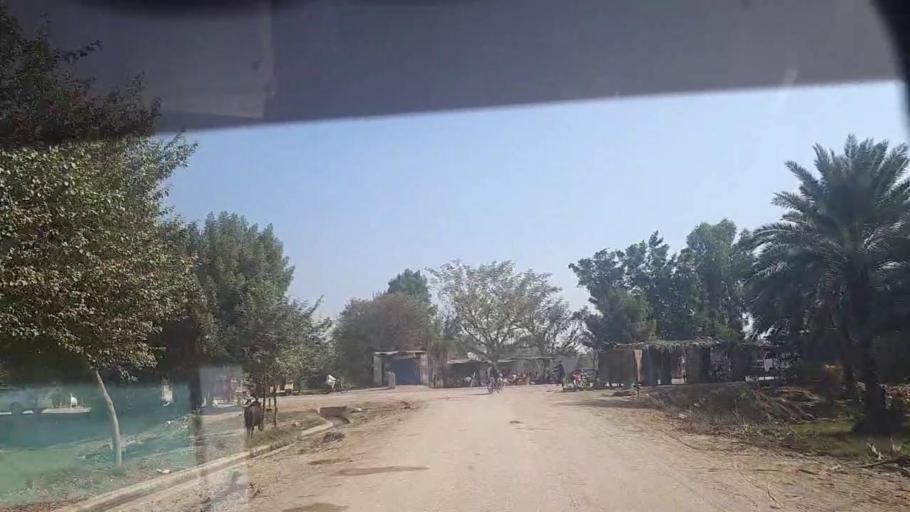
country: PK
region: Sindh
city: Khairpur
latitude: 27.4573
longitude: 68.7539
